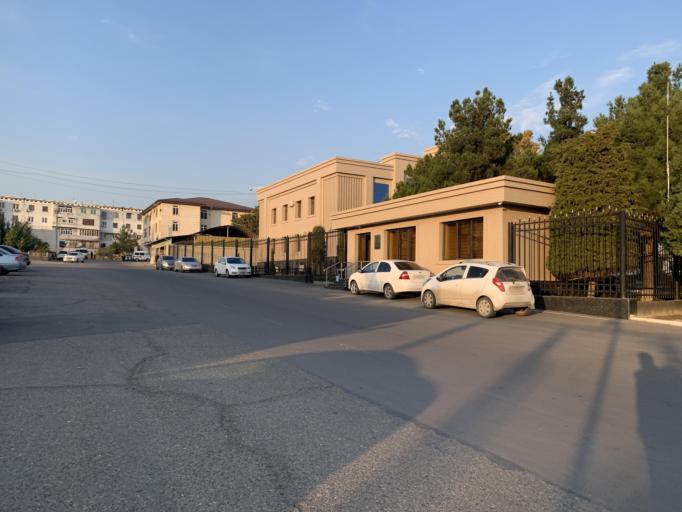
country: UZ
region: Namangan
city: Namangan Shahri
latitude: 41.0015
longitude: 71.6070
